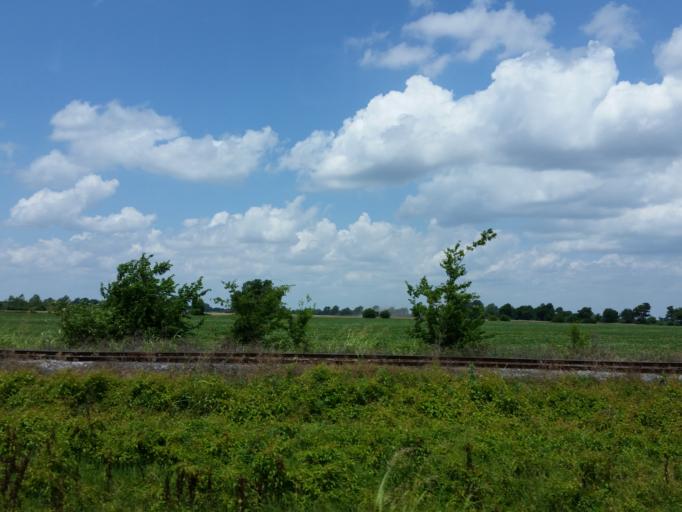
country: US
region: Tennessee
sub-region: Lake County
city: Tiptonville
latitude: 36.3954
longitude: -89.4591
